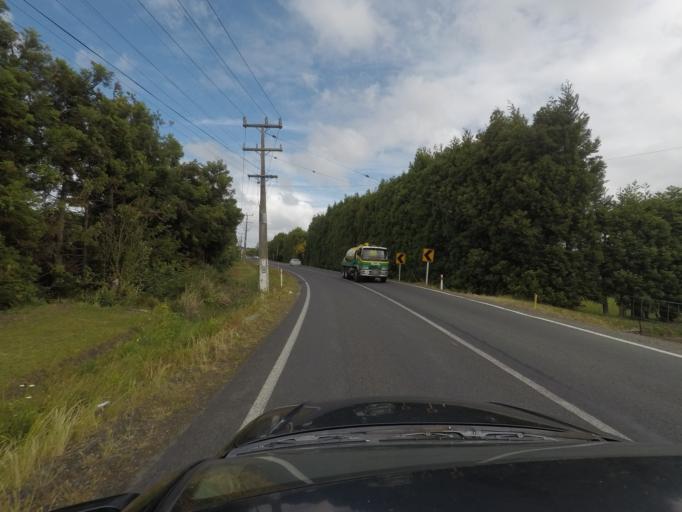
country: NZ
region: Auckland
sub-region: Auckland
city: Muriwai Beach
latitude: -36.7732
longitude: 174.5738
